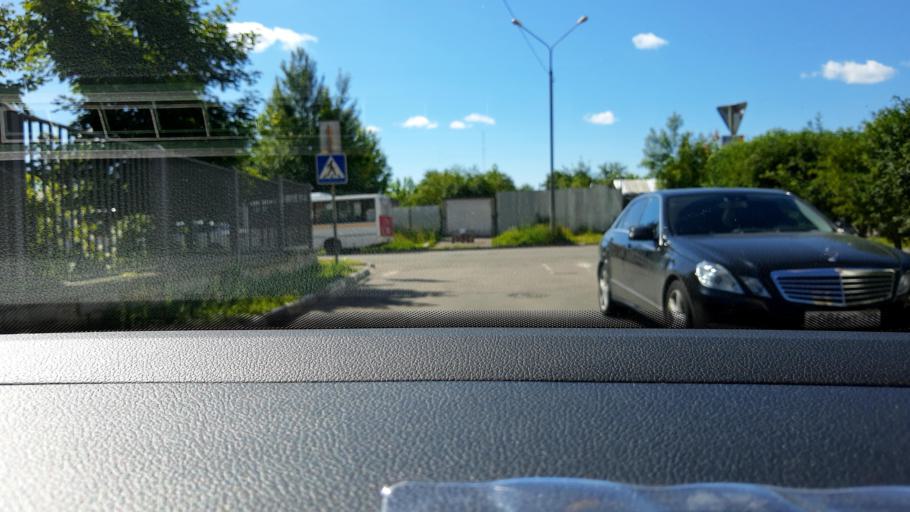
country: RU
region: Moscow
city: Vostochnyy
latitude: 55.8210
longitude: 37.8777
